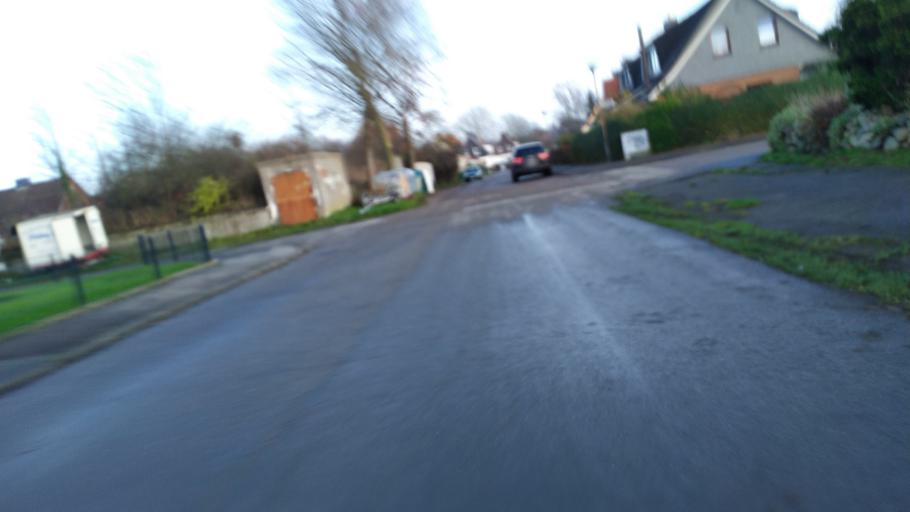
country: DE
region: Schleswig-Holstein
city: Travemuende
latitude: 53.9591
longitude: 10.8544
